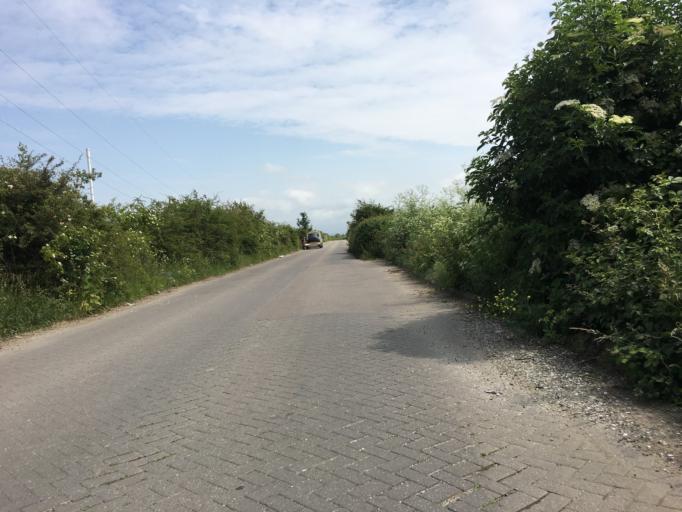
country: GB
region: England
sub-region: Kent
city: Queenborough
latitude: 51.3804
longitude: 0.7538
